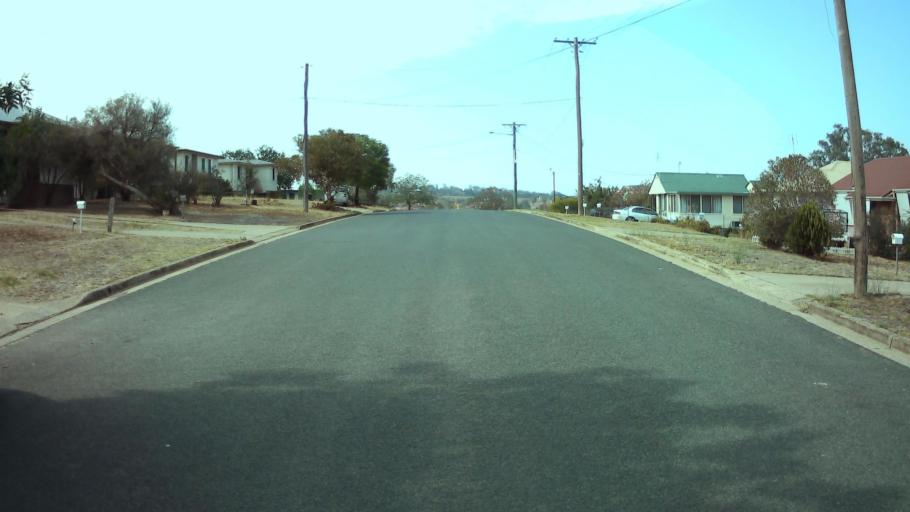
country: AU
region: New South Wales
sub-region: Weddin
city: Grenfell
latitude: -33.9015
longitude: 148.1572
